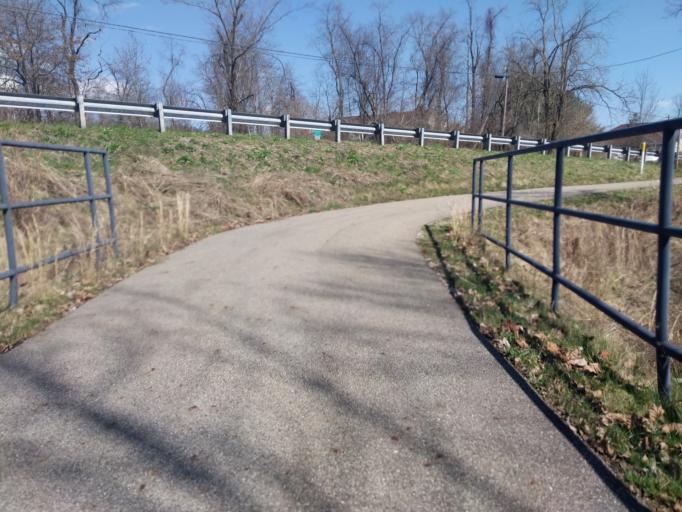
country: US
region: Ohio
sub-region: Athens County
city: The Plains
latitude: 39.3678
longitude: -82.1247
